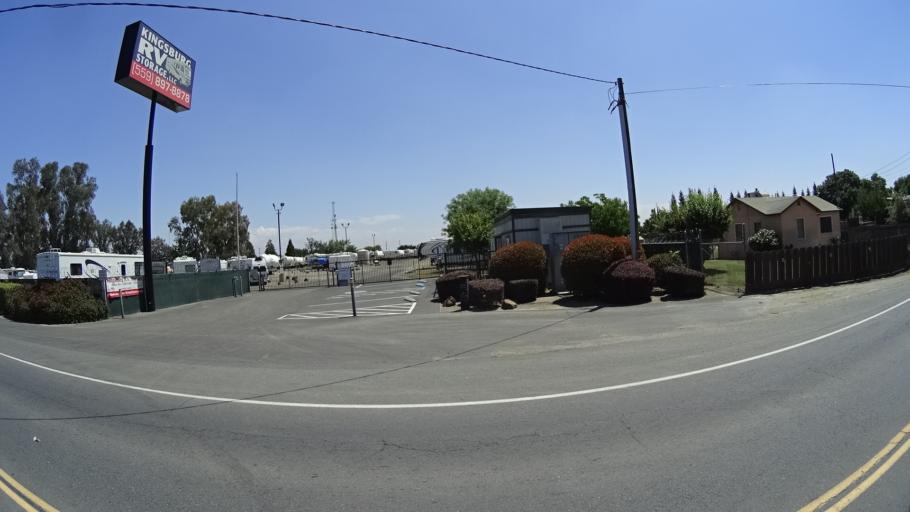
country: US
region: California
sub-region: Fresno County
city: Kingsburg
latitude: 36.5048
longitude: -119.5479
